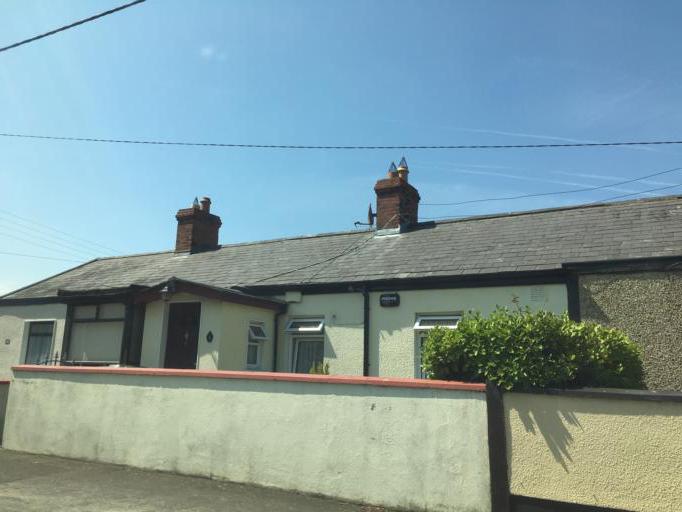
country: IE
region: Leinster
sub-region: Fingal County
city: Baldoyle
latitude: 53.3988
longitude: -6.1293
